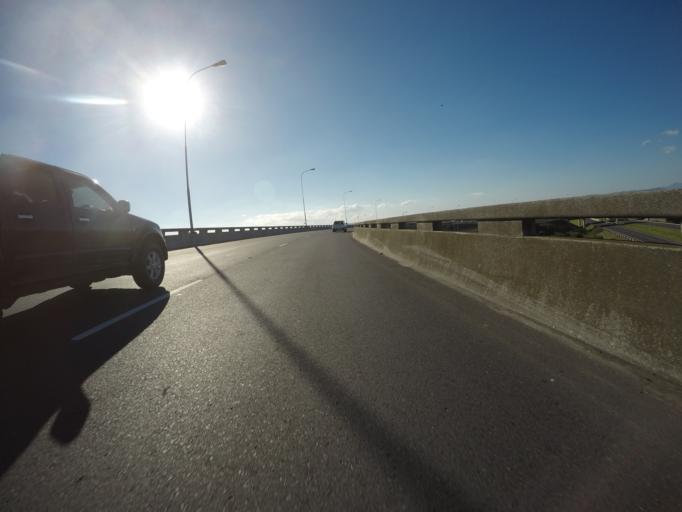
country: ZA
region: Western Cape
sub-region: City of Cape Town
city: Lansdowne
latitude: -34.0009
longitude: 18.6329
